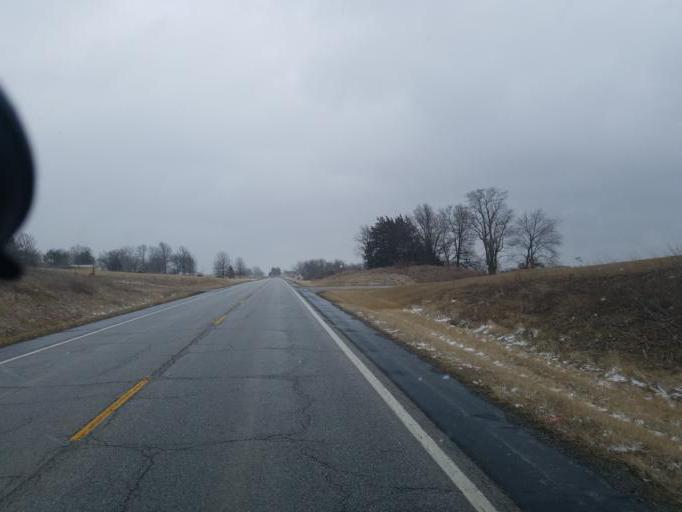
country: US
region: Missouri
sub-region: Putnam County
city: Unionville
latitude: 40.4689
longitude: -92.9299
